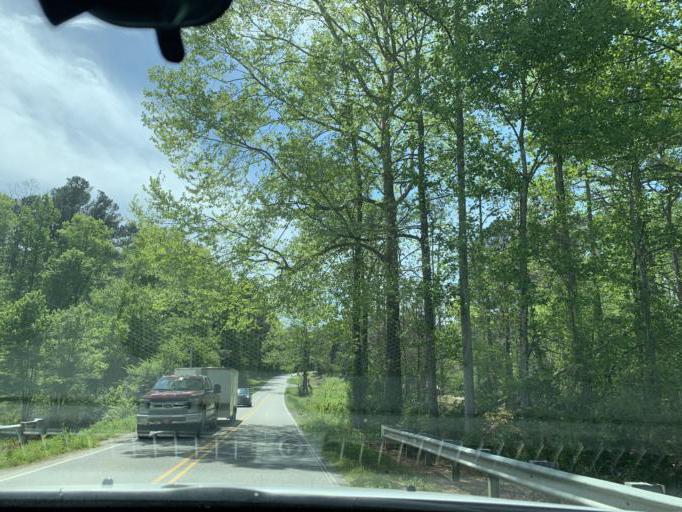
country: US
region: Georgia
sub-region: Forsyth County
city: Cumming
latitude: 34.2720
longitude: -84.1910
